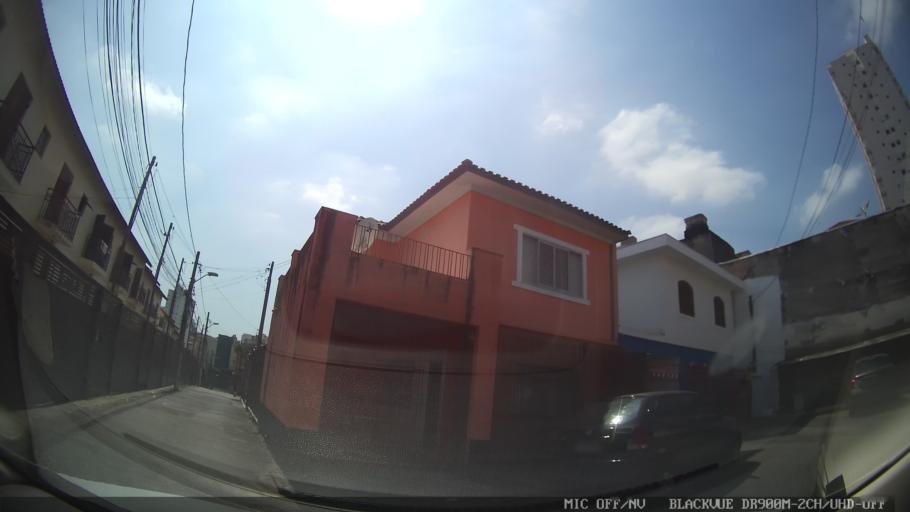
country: BR
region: Sao Paulo
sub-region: Sao Paulo
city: Sao Paulo
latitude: -23.4881
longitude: -46.6446
